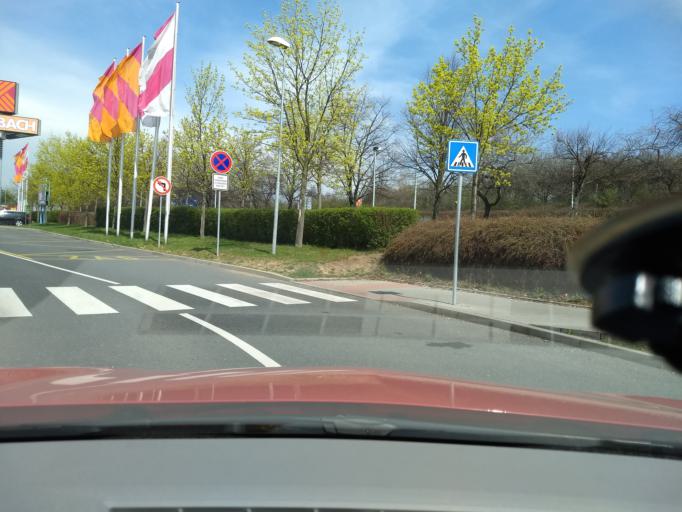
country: CZ
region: Central Bohemia
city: Hostivice
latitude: 50.0746
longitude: 14.3096
